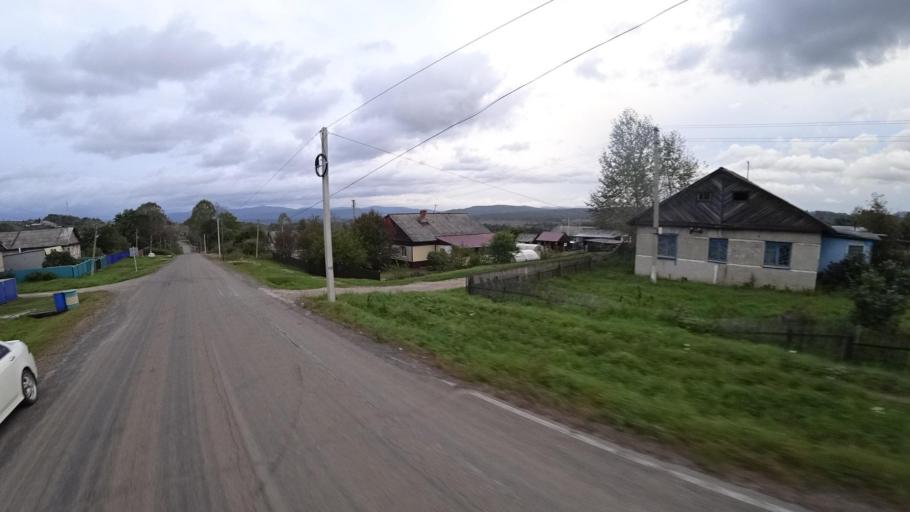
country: RU
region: Jewish Autonomous Oblast
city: Izvestkovyy
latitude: 48.9692
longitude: 131.5855
